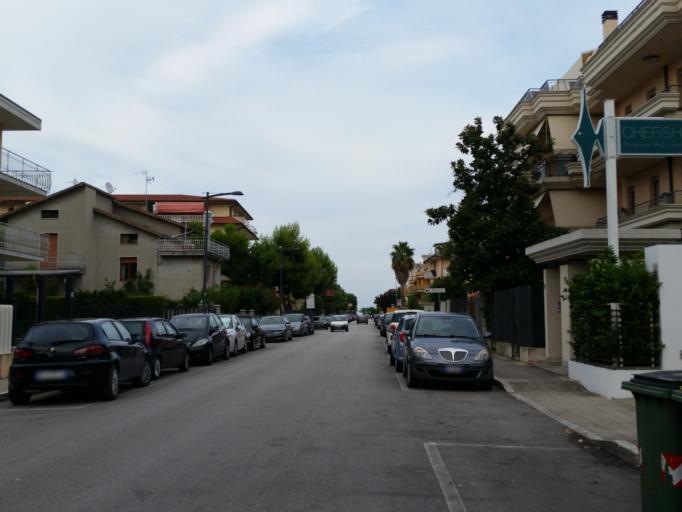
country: IT
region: The Marches
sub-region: Provincia di Ascoli Piceno
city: San Benedetto del Tronto
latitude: 42.9102
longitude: 13.9024
